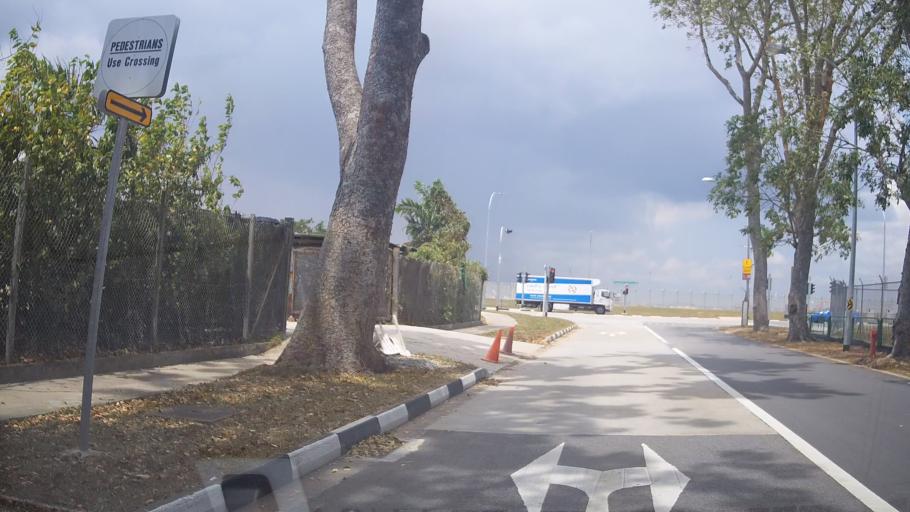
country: SG
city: Singapore
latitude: 1.3201
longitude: 103.9795
